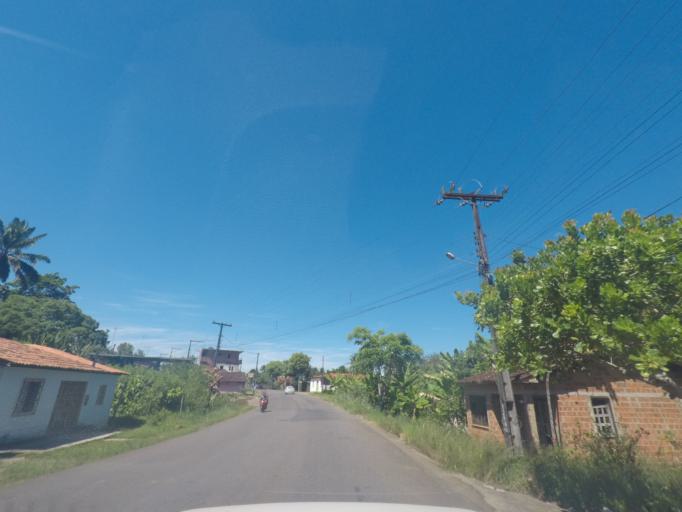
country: BR
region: Bahia
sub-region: Valenca
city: Valenca
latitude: -13.4162
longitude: -39.0762
